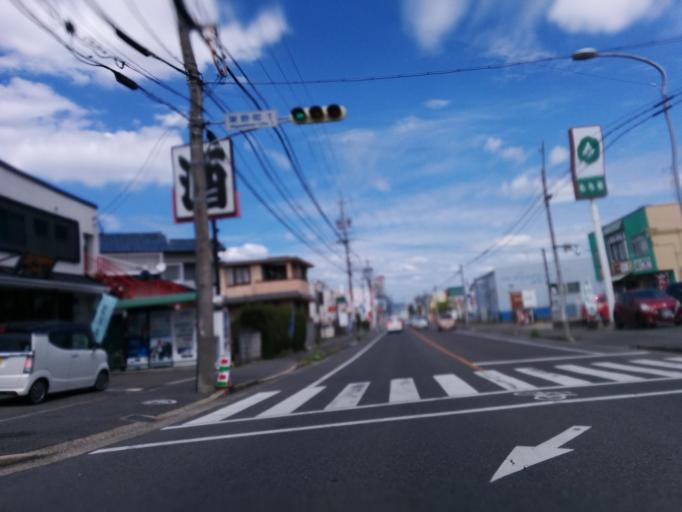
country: JP
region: Aichi
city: Kasugai
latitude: 35.2616
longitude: 136.9793
